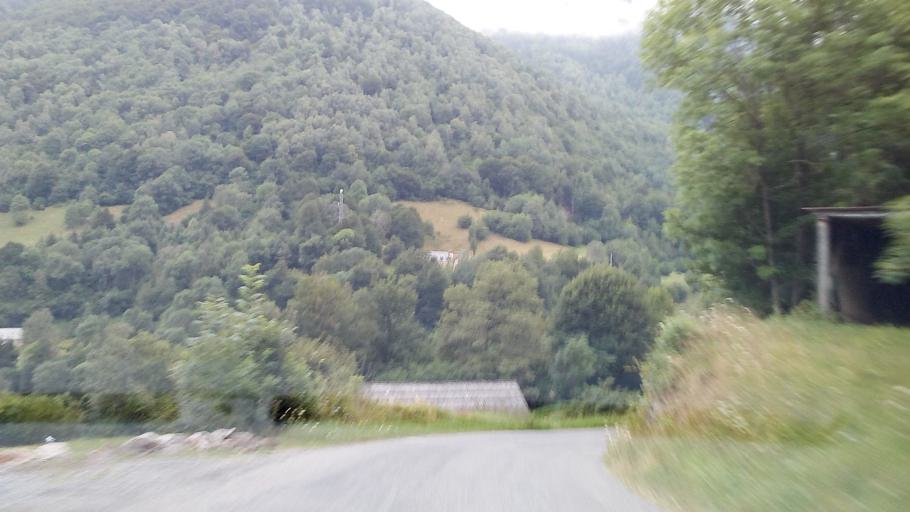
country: FR
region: Midi-Pyrenees
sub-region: Departement des Hautes-Pyrenees
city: Cauterets
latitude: 42.9422
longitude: -0.1796
